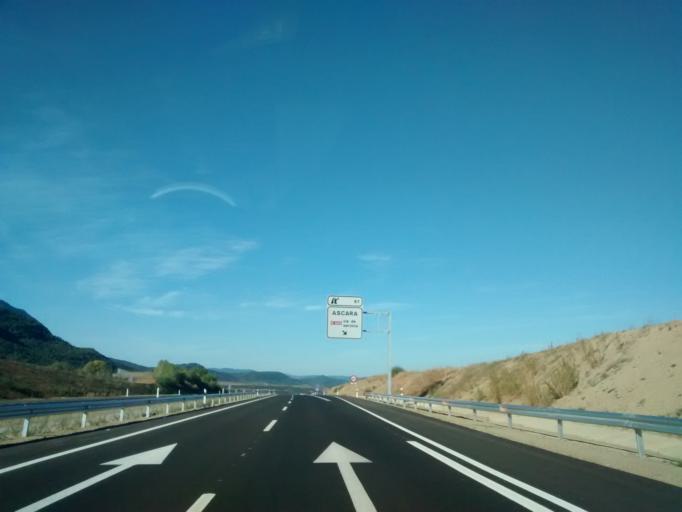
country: ES
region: Aragon
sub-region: Provincia de Huesca
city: Santa Cruz de la Seros
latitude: 42.5630
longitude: -0.6441
